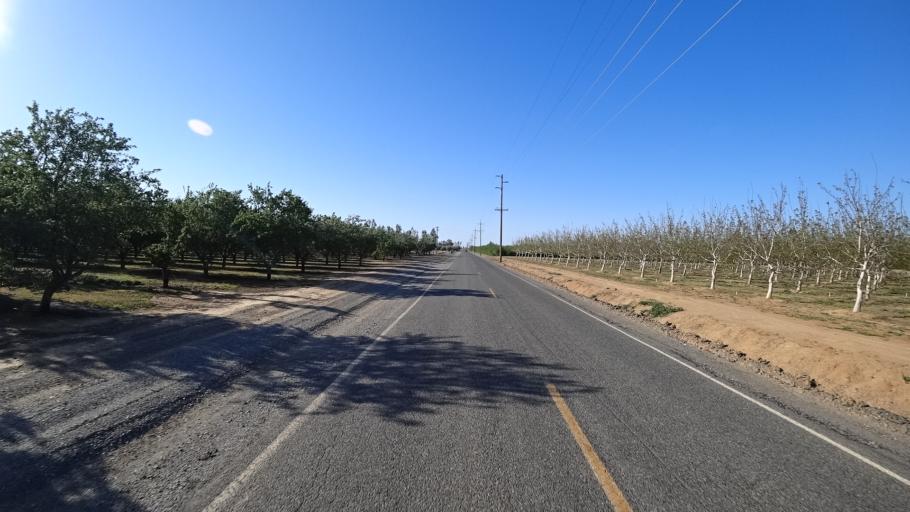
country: US
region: California
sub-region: Glenn County
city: Orland
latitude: 39.7051
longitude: -122.1782
